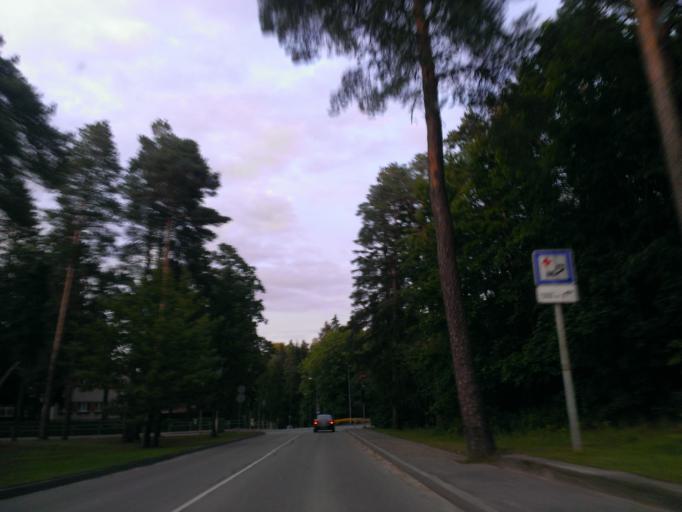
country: LV
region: Ogre
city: Ogre
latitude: 56.8195
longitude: 24.6105
